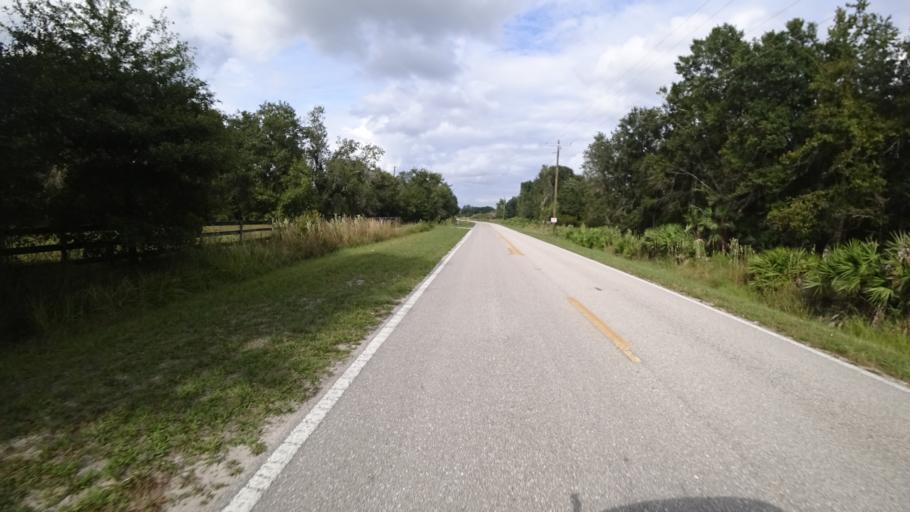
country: US
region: Florida
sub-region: Hillsborough County
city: Wimauma
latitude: 27.5832
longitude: -82.1994
